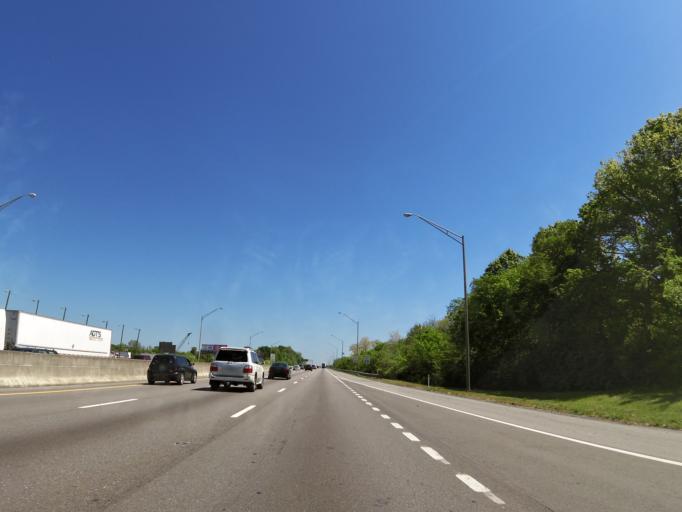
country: US
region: Tennessee
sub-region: Knox County
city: Knoxville
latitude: 35.9945
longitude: -83.8968
